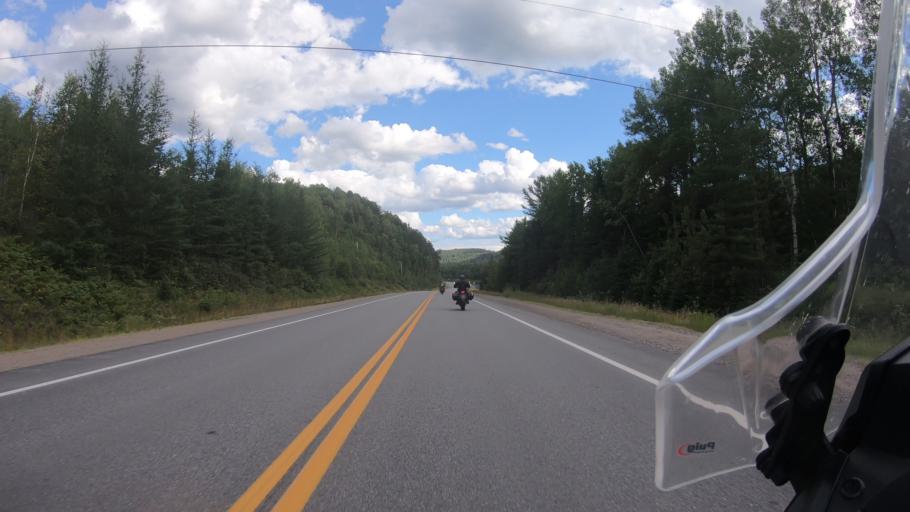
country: CA
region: Quebec
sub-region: Mauricie
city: Saint-Tite
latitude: 47.0026
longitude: -72.9253
